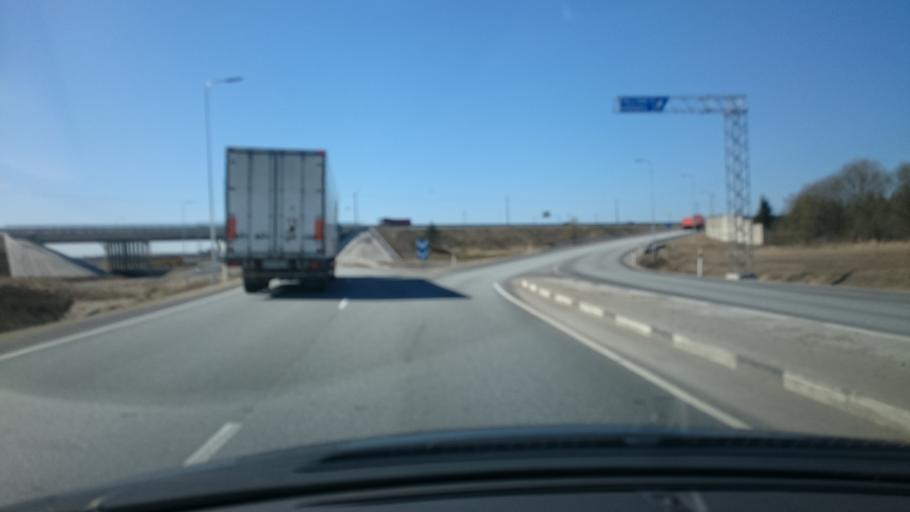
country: EE
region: Harju
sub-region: Rae vald
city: Jueri
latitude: 59.3550
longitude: 24.8824
